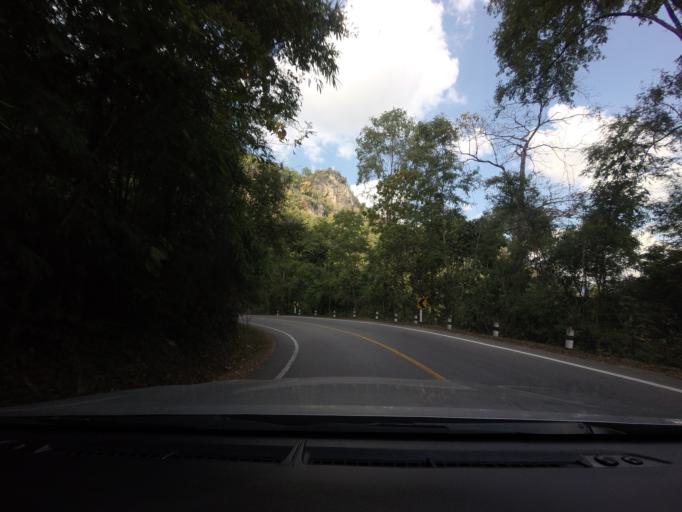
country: TH
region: Chiang Mai
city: Chai Prakan
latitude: 19.5961
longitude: 99.1125
